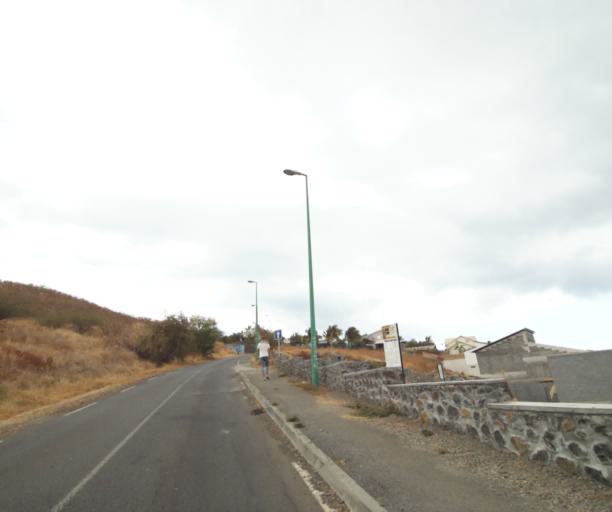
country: RE
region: Reunion
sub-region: Reunion
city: Saint-Paul
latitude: -21.0600
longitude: 55.2318
